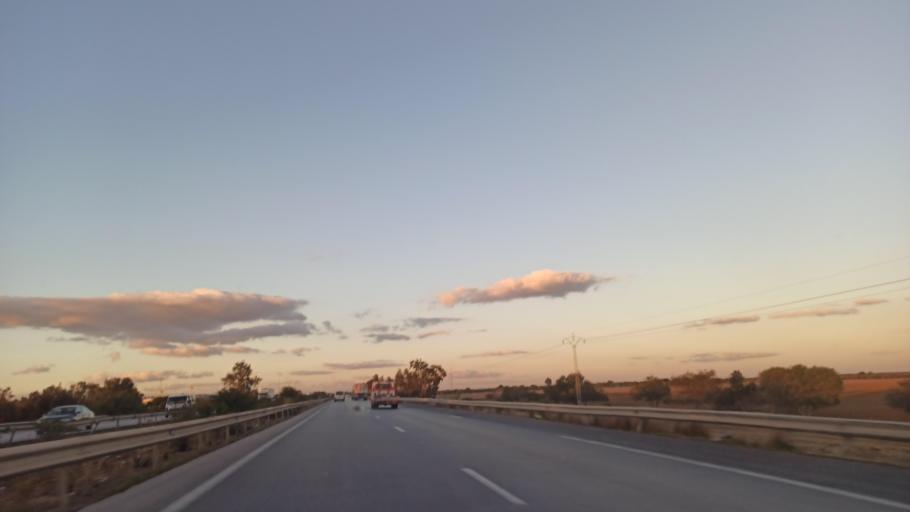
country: TN
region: Susah
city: Harqalah
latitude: 36.1277
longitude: 10.4065
